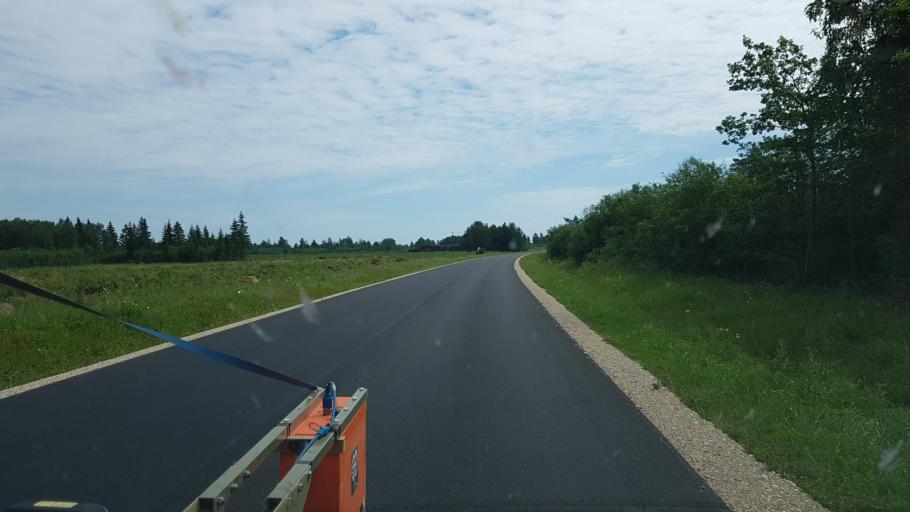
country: EE
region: Paernumaa
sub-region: Halinga vald
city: Parnu-Jaagupi
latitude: 58.6195
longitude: 24.2812
